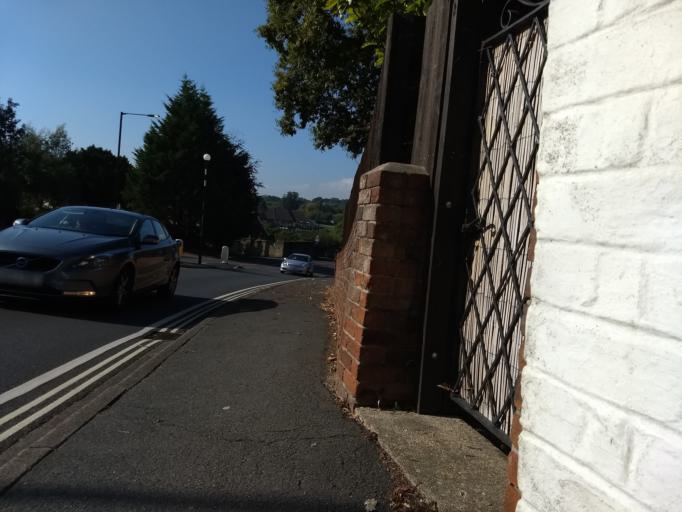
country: GB
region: England
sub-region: Isle of Wight
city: Newchurch
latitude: 50.7248
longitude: -1.2238
